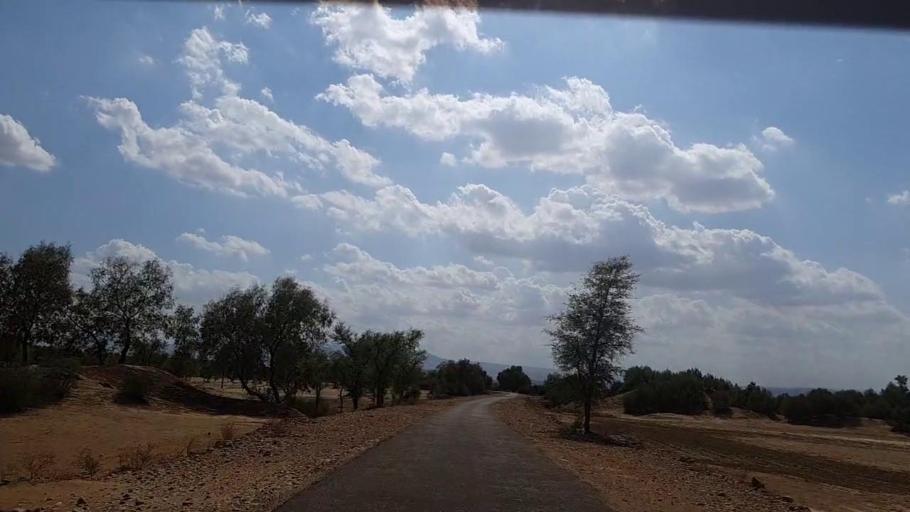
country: PK
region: Sindh
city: Johi
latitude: 26.5203
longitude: 67.4574
